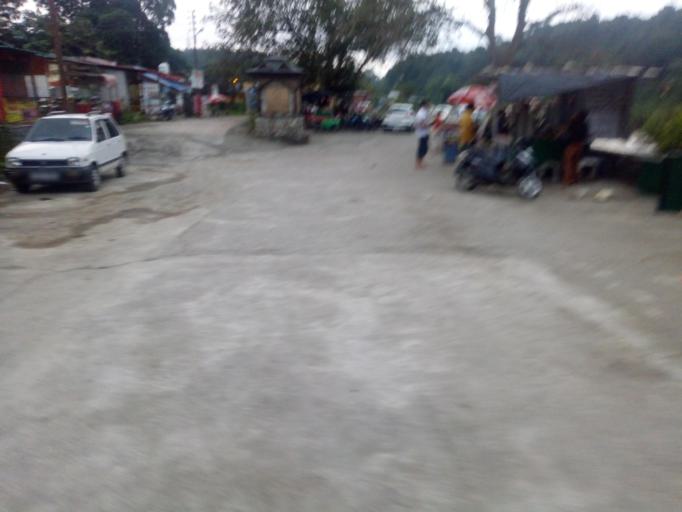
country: IN
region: Uttarakhand
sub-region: Dehradun
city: Dehradun
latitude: 30.3752
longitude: 78.0593
